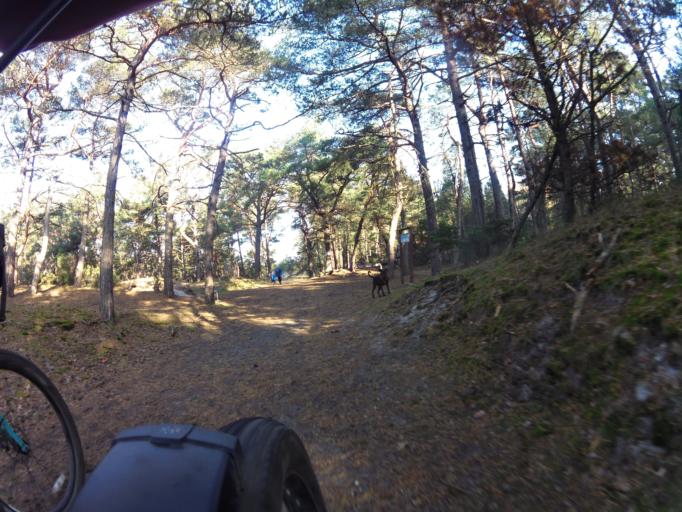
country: PL
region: Pomeranian Voivodeship
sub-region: Powiat pucki
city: Hel
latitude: 54.6047
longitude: 18.8181
